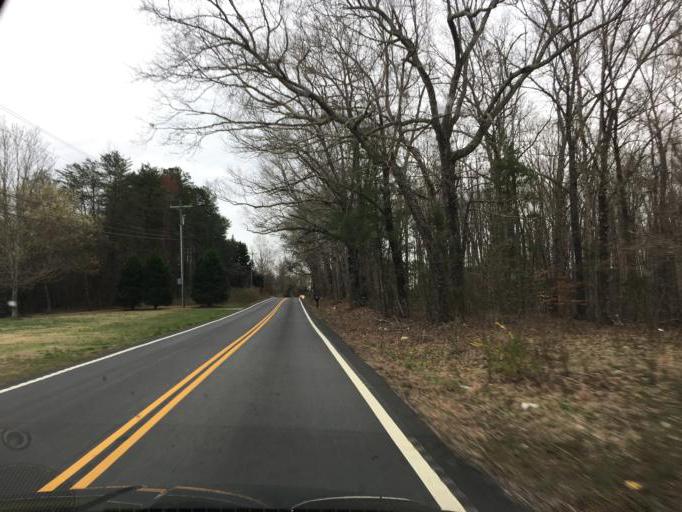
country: US
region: South Carolina
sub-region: Greenville County
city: Berea
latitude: 34.9227
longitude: -82.4824
